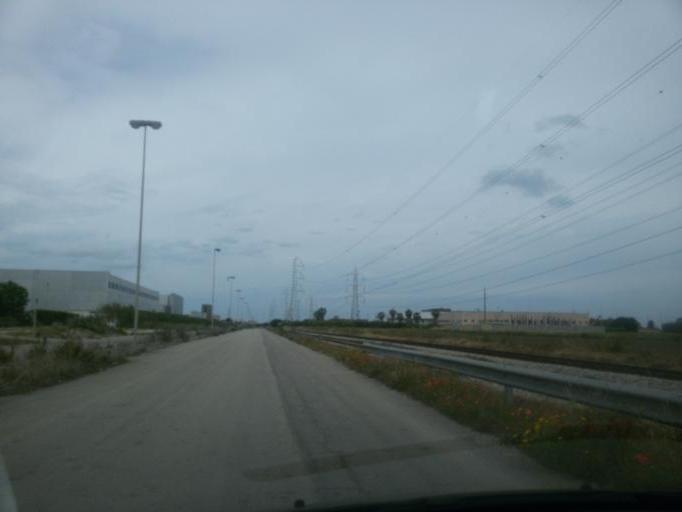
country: IT
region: Apulia
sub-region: Provincia di Brindisi
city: Materdomini
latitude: 40.6288
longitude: 17.9803
